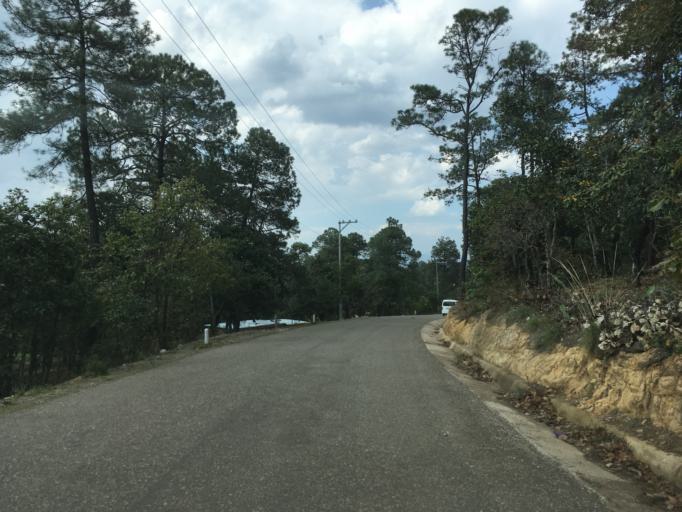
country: MX
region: Oaxaca
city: Santiago Tilantongo
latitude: 17.2139
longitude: -97.2817
